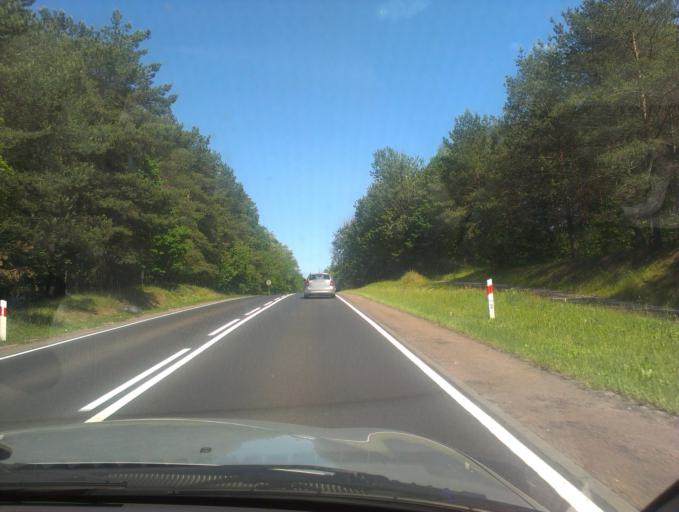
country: PL
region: Pomeranian Voivodeship
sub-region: Powiat czluchowski
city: Czluchow
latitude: 53.6797
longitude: 17.4014
